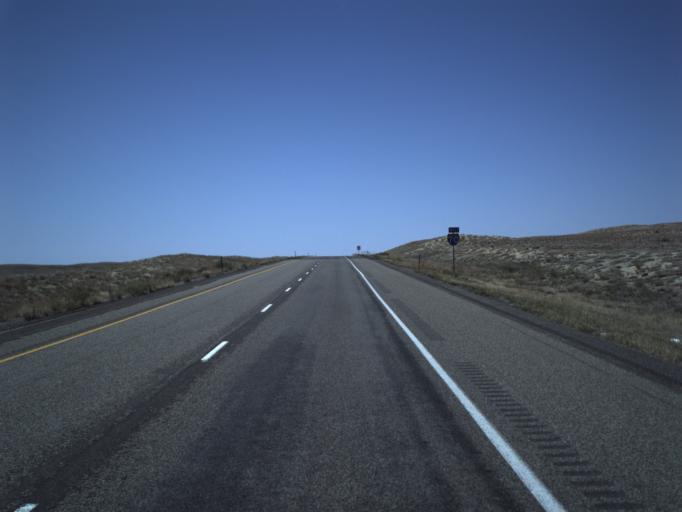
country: US
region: Colorado
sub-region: Mesa County
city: Loma
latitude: 39.1082
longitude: -109.1917
